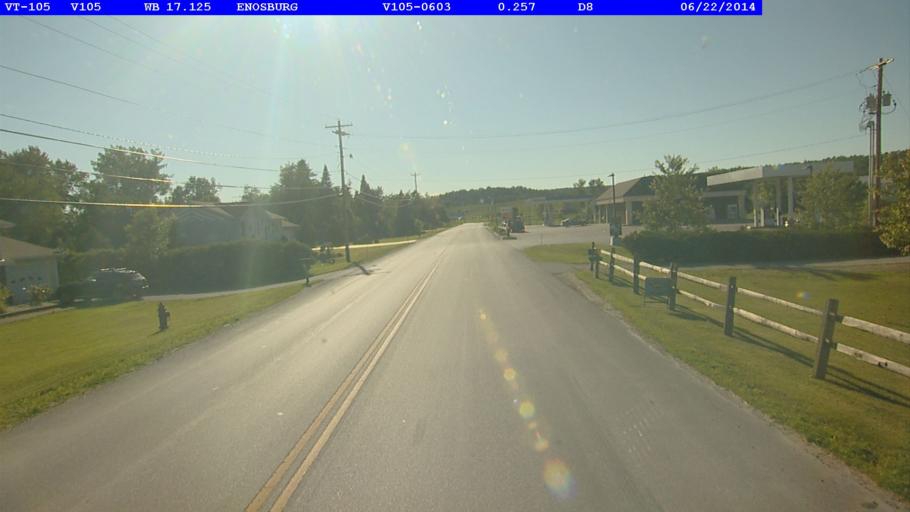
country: US
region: Vermont
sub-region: Franklin County
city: Enosburg Falls
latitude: 44.9063
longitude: -72.8149
